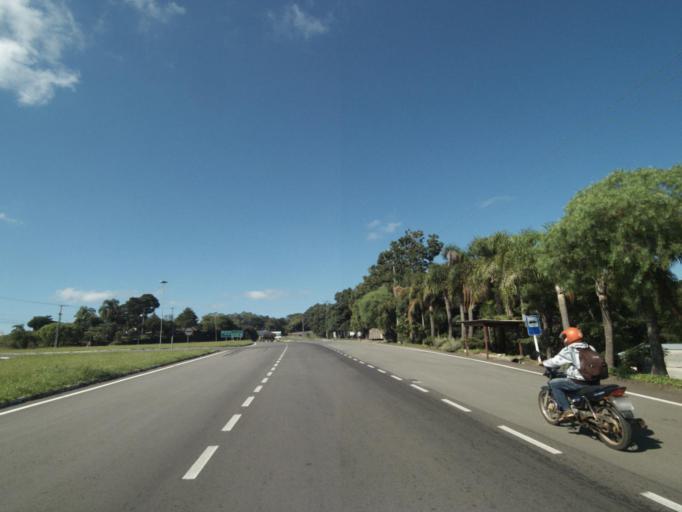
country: BR
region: Rio Grande do Sul
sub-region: Bento Goncalves
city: Bento Goncalves
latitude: -29.1190
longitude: -51.5424
